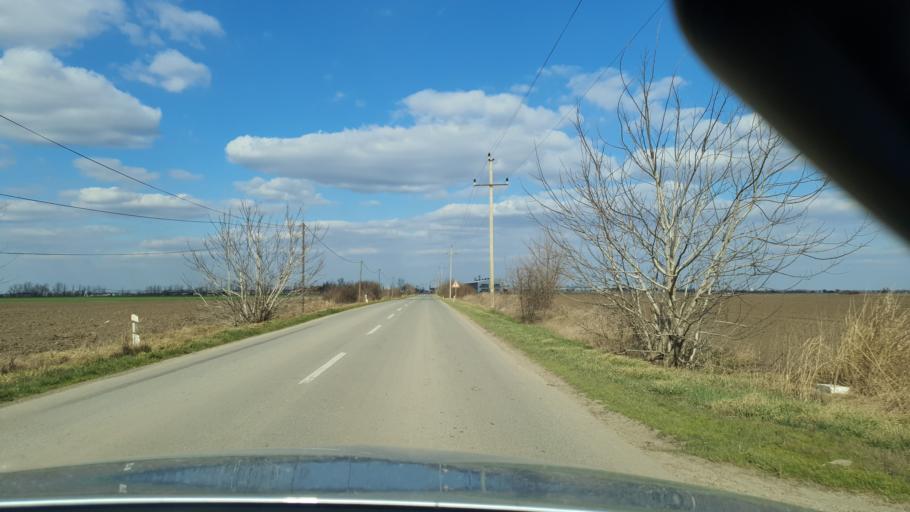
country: RS
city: Kulpin
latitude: 45.4143
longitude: 19.5947
